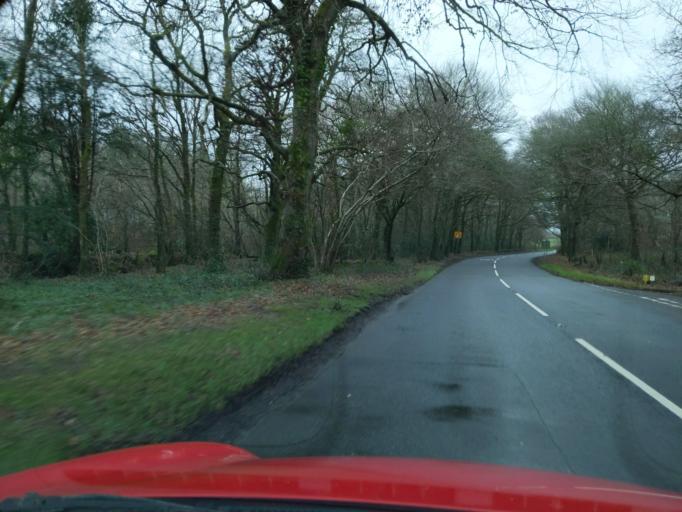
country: GB
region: England
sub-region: Cornwall
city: Werrington
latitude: 50.6956
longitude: -4.3231
